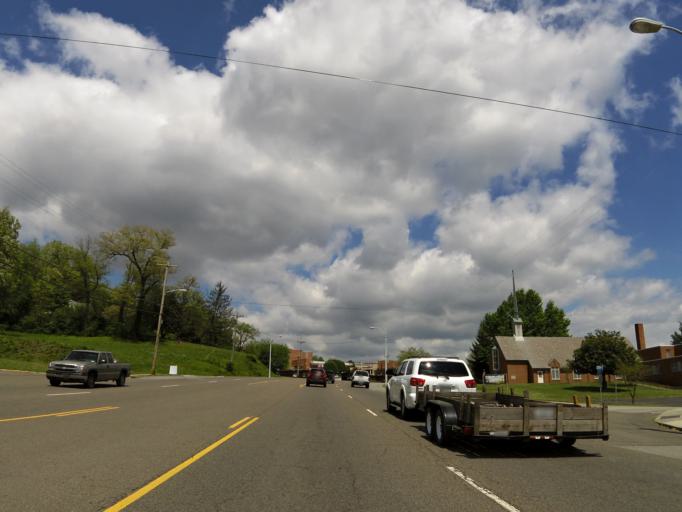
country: US
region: Tennessee
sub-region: Campbell County
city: LaFollette
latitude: 36.3870
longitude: -84.1148
